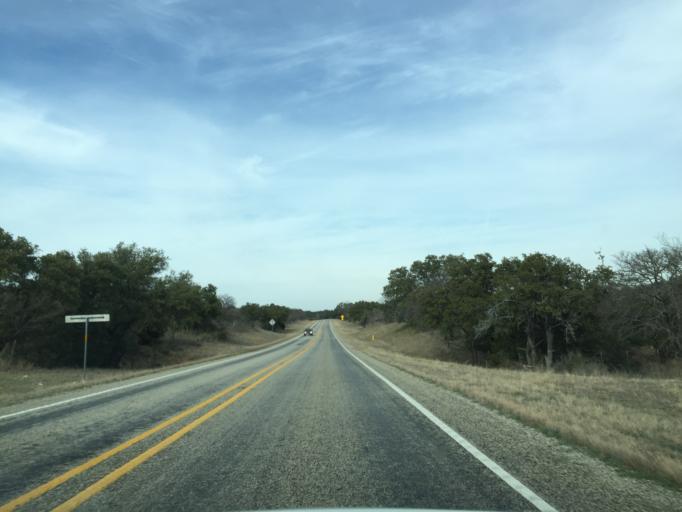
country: US
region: Texas
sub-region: Gillespie County
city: Fredericksburg
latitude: 30.4856
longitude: -98.7041
